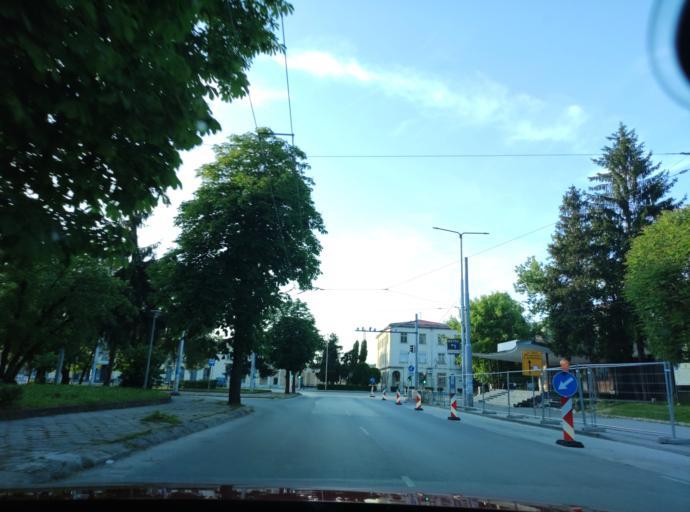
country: BG
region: Pleven
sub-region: Obshtina Pleven
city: Pleven
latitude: 43.4197
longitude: 24.6153
